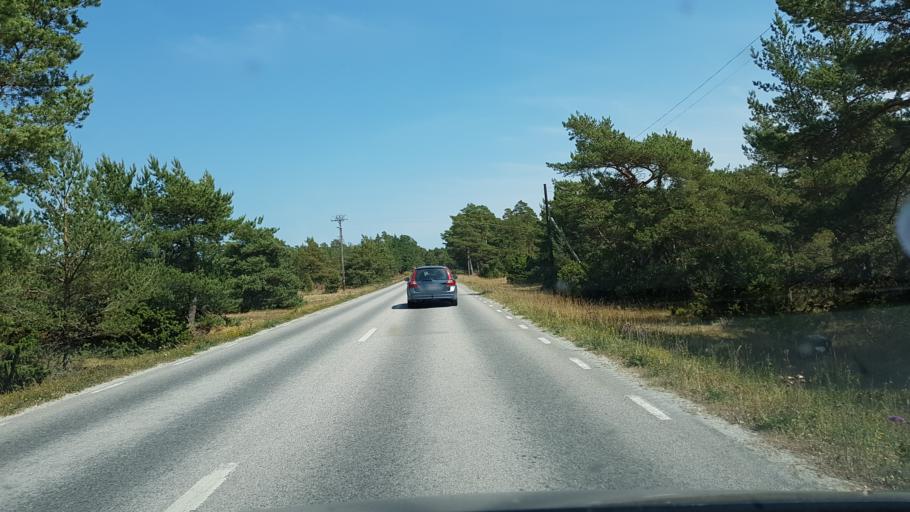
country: SE
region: Gotland
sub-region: Gotland
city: Visby
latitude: 57.6382
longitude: 18.3912
